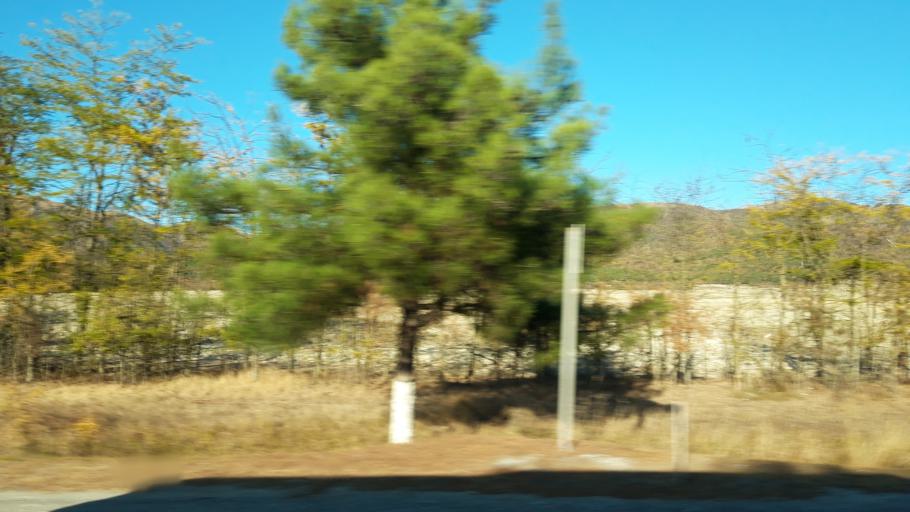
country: RU
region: Krasnodarskiy
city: Kabardinka
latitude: 44.6330
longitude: 37.9995
